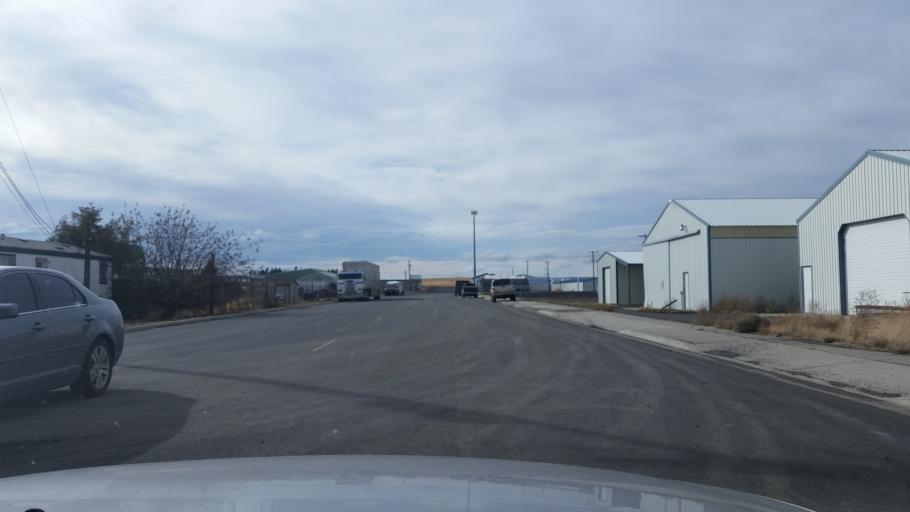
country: US
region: Washington
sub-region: Lincoln County
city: Davenport
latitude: 47.6460
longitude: -118.1552
